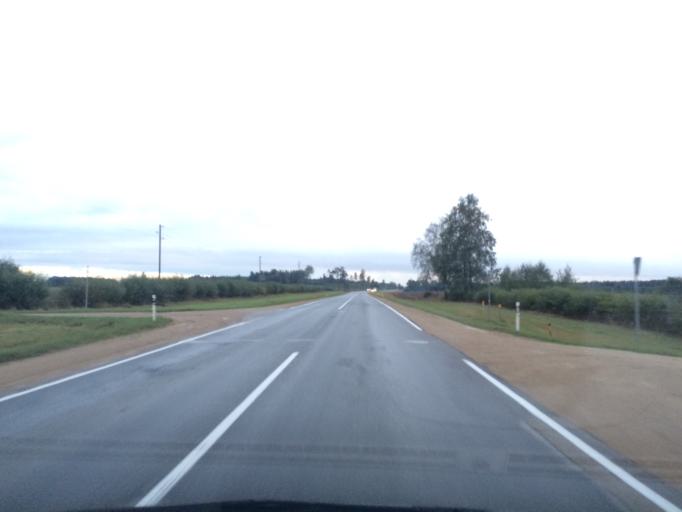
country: LV
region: Plavinu
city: Plavinas
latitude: 56.5774
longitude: 25.7772
